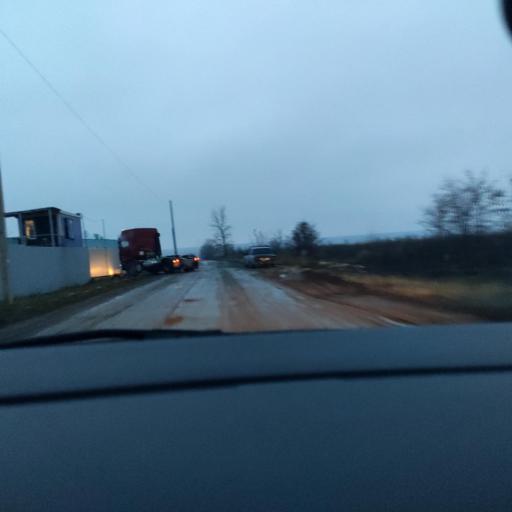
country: RU
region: Voronezj
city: Shilovo
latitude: 51.5718
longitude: 39.1359
